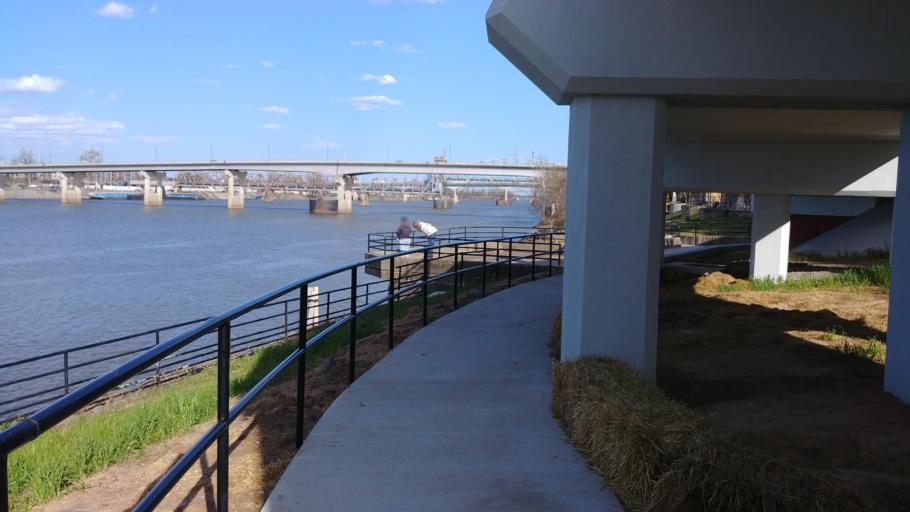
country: US
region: Arkansas
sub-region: Pulaski County
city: Little Rock
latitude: 34.7501
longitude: -92.2732
